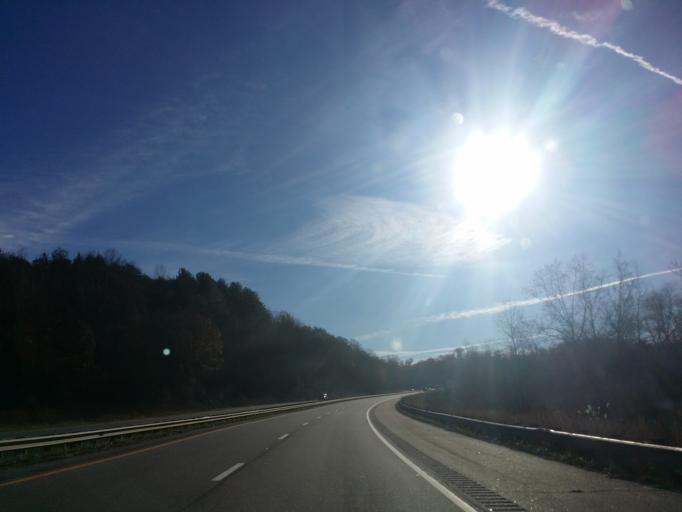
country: US
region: North Carolina
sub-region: McDowell County
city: West Marion
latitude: 35.6401
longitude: -82.1131
